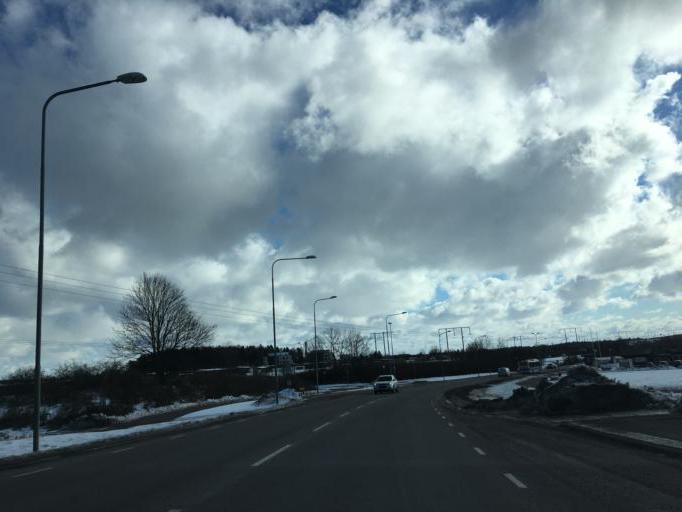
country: SE
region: Vaestmanland
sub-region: Vasteras
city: Vasteras
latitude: 59.6026
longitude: 16.4581
